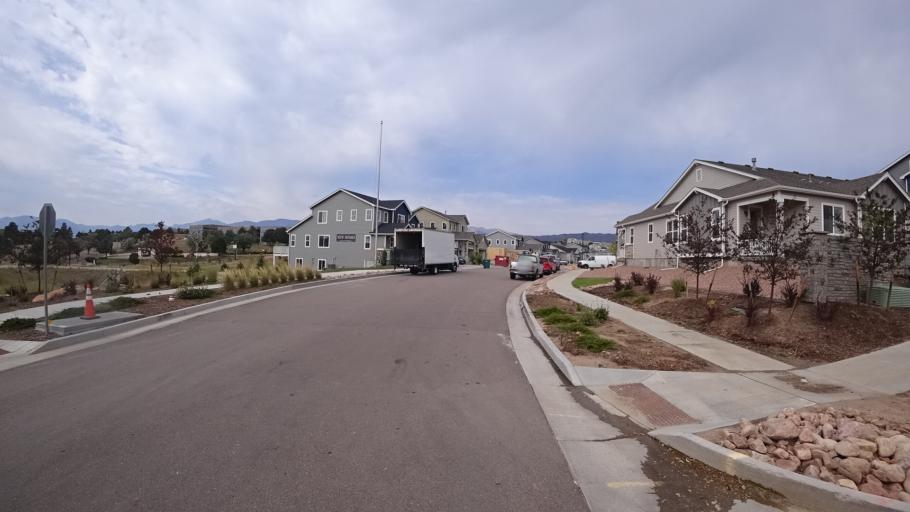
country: US
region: Colorado
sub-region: El Paso County
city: Colorado Springs
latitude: 38.9160
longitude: -104.8238
